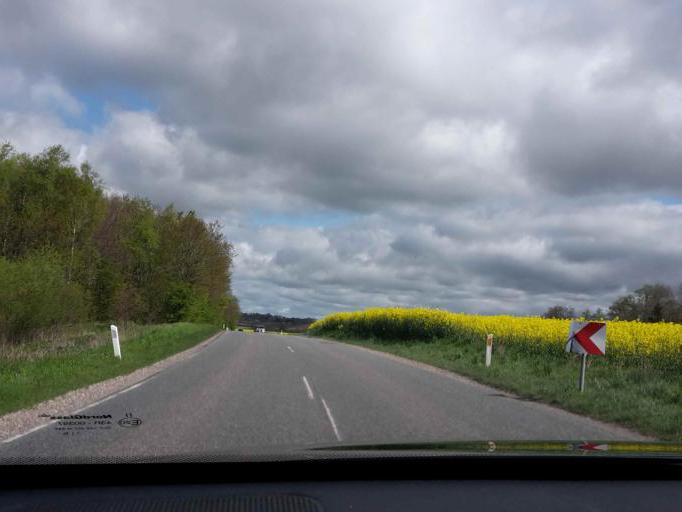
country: DK
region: Central Jutland
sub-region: Syddjurs Kommune
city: Hornslet
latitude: 56.3350
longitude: 10.3349
